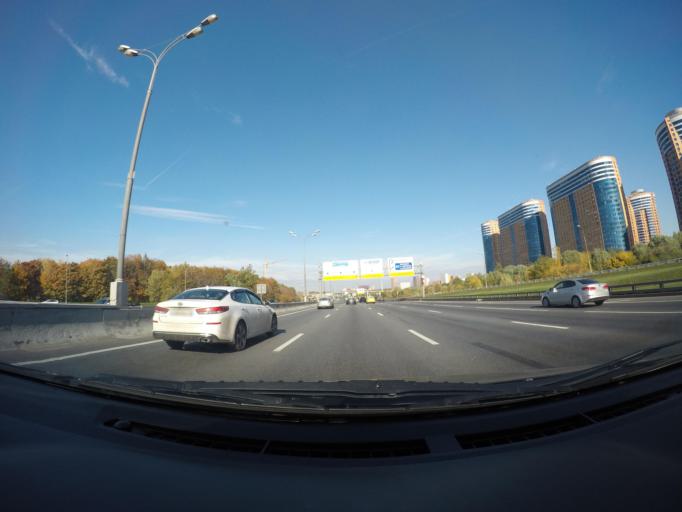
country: RU
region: Moscow
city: Ivanovskoye
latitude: 55.7708
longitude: 37.8435
